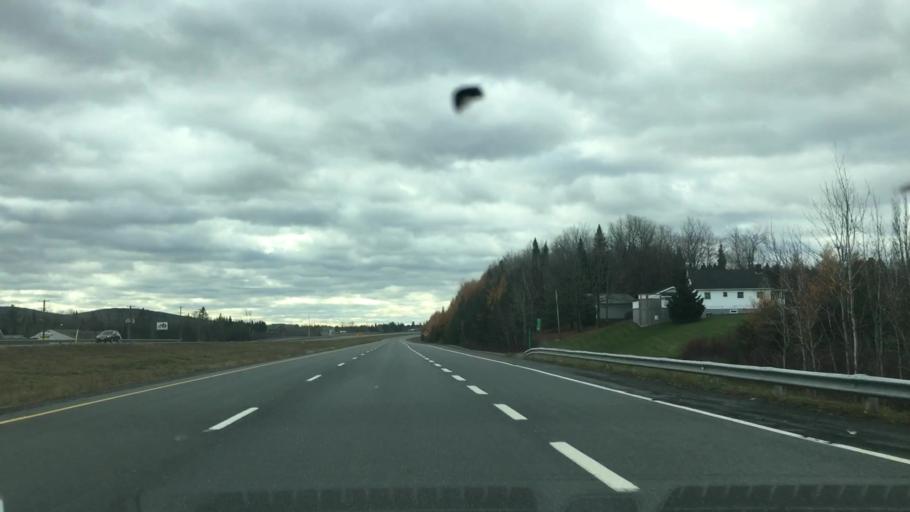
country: US
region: Maine
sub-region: Aroostook County
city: Fort Fairfield
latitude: 46.7478
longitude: -67.7147
